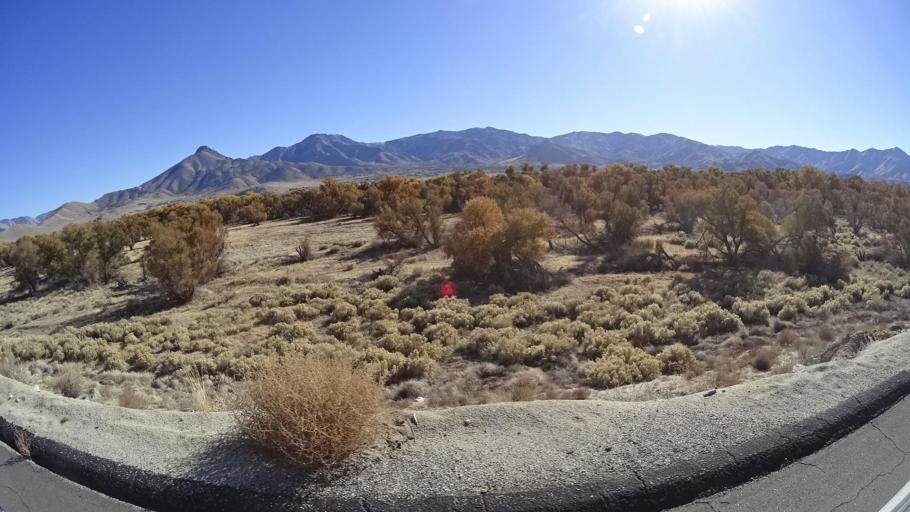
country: US
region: California
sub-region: Kern County
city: Weldon
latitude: 35.6725
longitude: -118.3486
